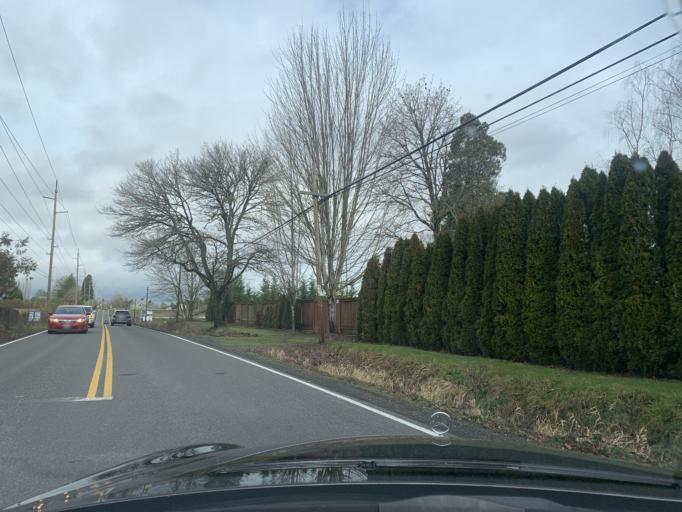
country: US
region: Oregon
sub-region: Multnomah County
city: Gresham
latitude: 45.4675
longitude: -122.4667
